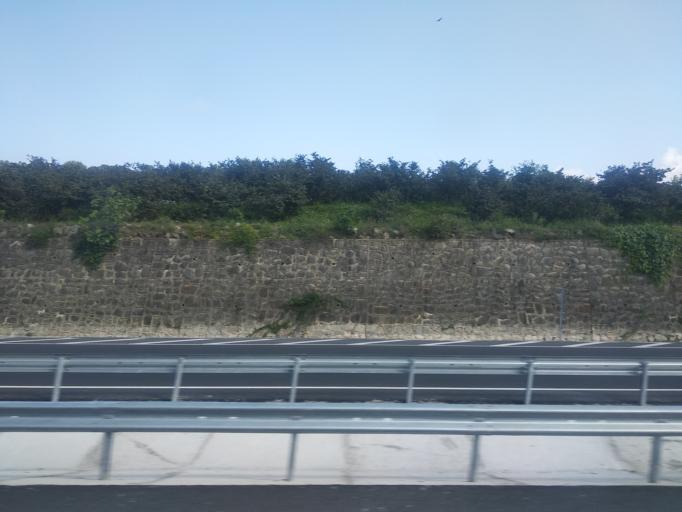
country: TR
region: Ordu
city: Ordu
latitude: 40.9918
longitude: 37.8151
